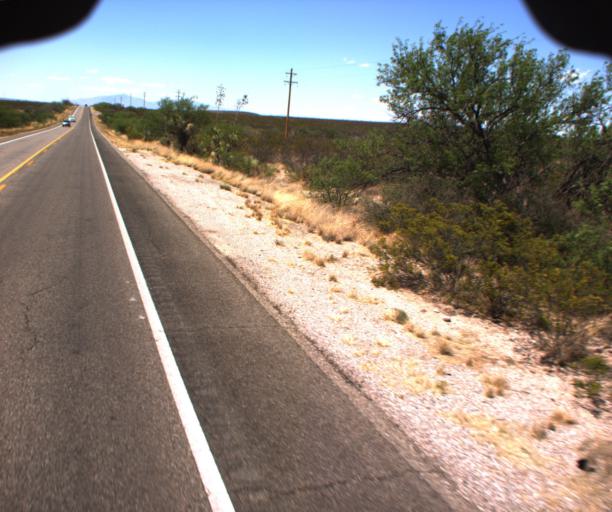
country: US
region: Arizona
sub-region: Cochise County
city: Tombstone
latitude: 31.7638
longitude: -110.1159
